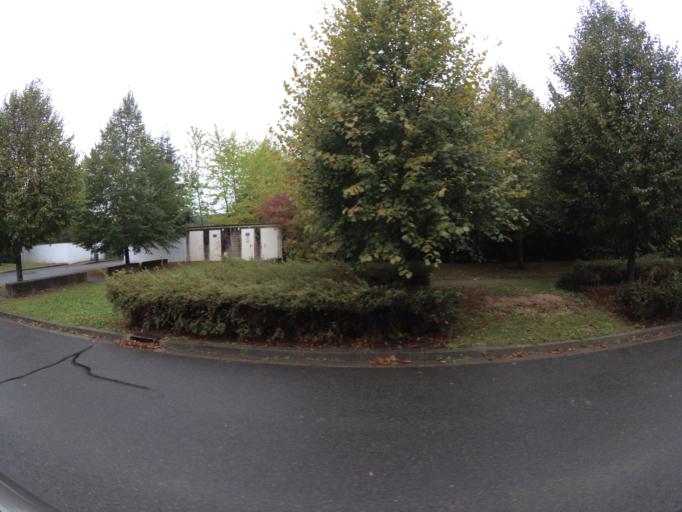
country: FR
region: Ile-de-France
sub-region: Departement de Seine-et-Marne
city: Chanteloup-en-Brie
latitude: 48.8326
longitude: 2.7311
